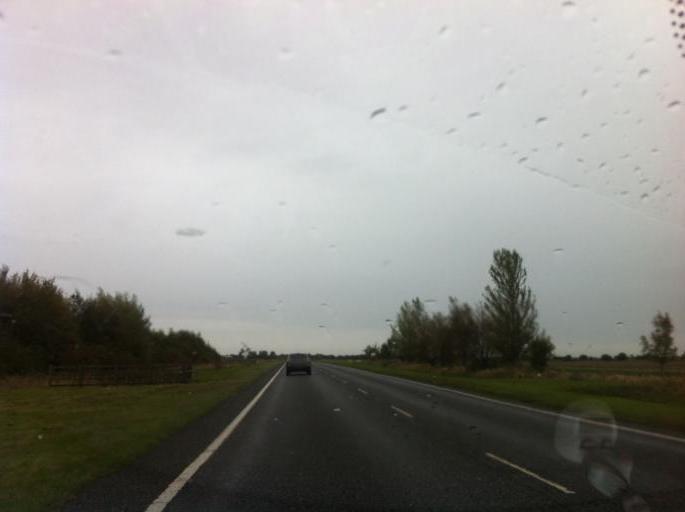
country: GB
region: England
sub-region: Lincolnshire
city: Spalding
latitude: 52.7280
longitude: -0.1236
